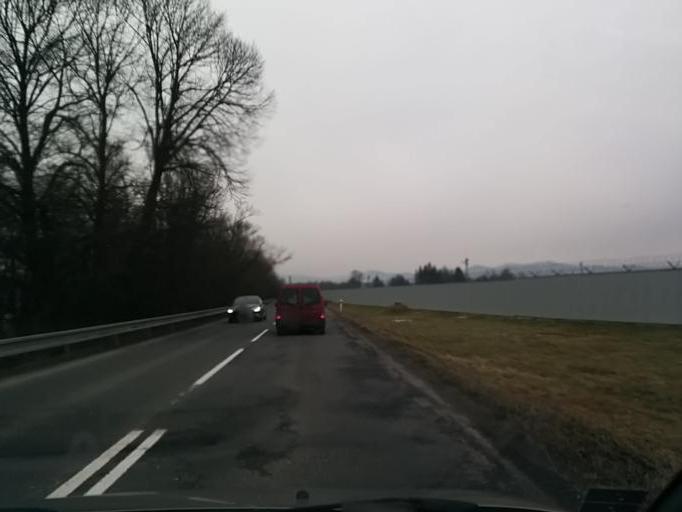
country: SK
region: Banskobystricky
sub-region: Okres Banska Bystrica
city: Zvolen
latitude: 48.6285
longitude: 19.1398
